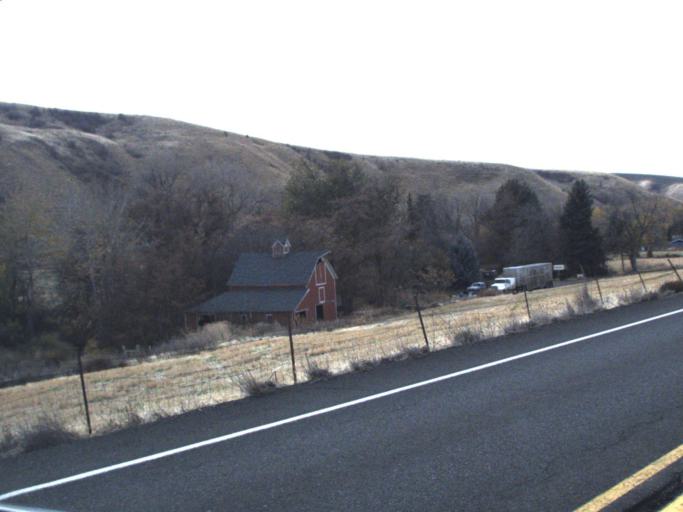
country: US
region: Washington
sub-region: Garfield County
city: Pomeroy
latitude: 46.4723
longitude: -117.5285
